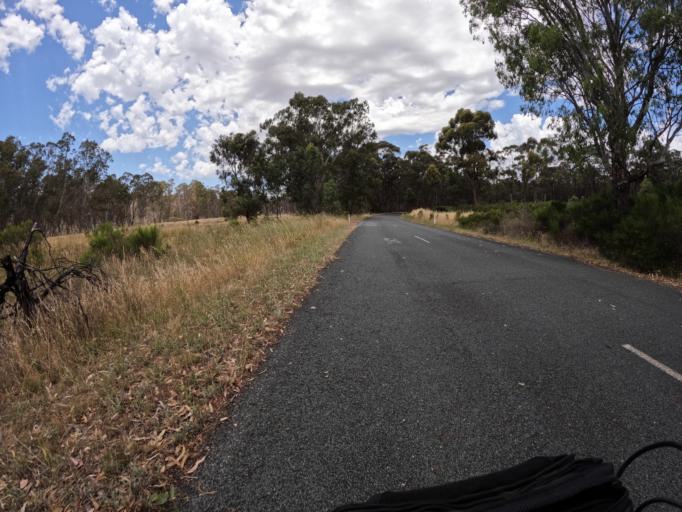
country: AU
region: Victoria
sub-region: Greater Shepparton
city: Shepparton
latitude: -36.6868
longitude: 145.1805
